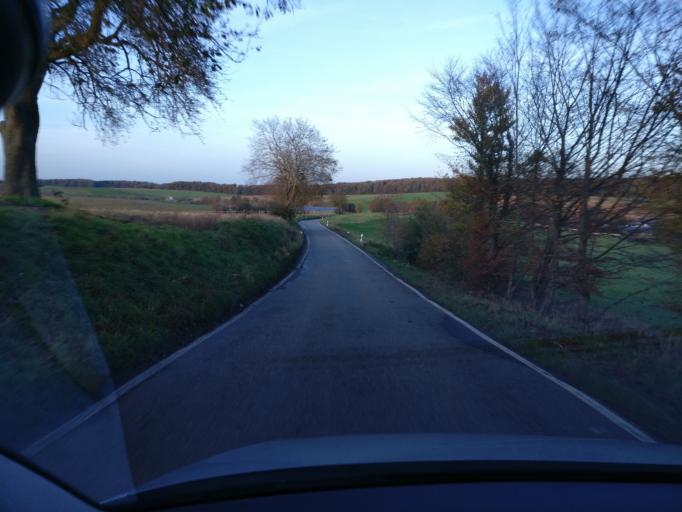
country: DE
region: Baden-Wuerttemberg
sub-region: Karlsruhe Region
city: Woessingen
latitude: 49.0406
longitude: 8.6050
